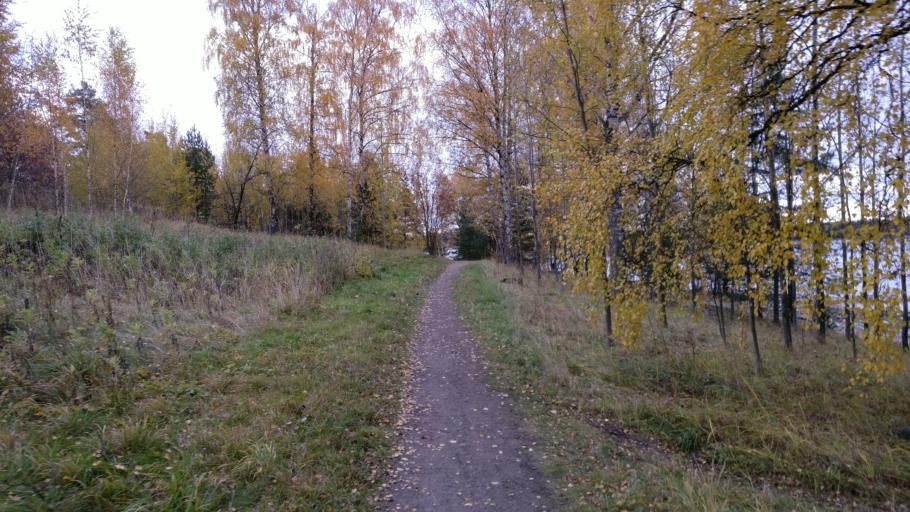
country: FI
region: Uusimaa
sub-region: Helsinki
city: Helsinki
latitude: 60.1784
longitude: 24.9903
